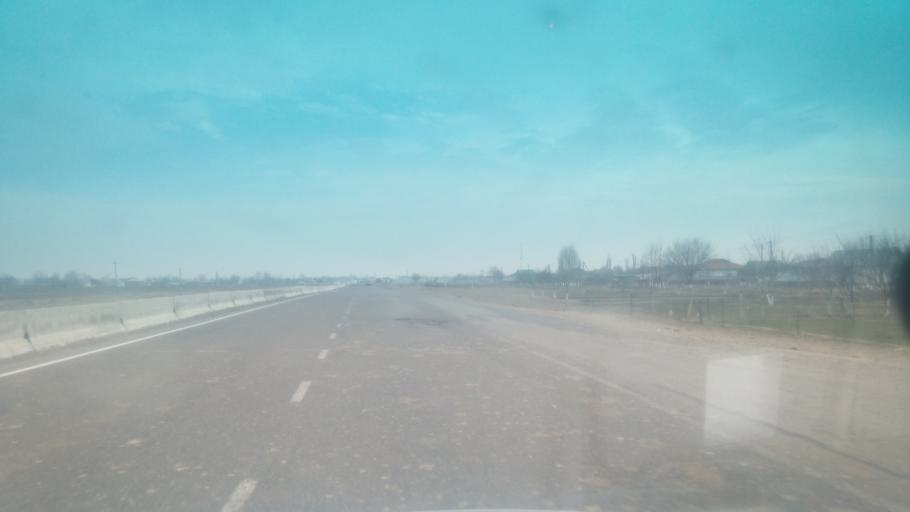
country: KZ
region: Ongtustik Qazaqstan
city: Myrzakent
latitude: 40.5080
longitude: 68.5071
